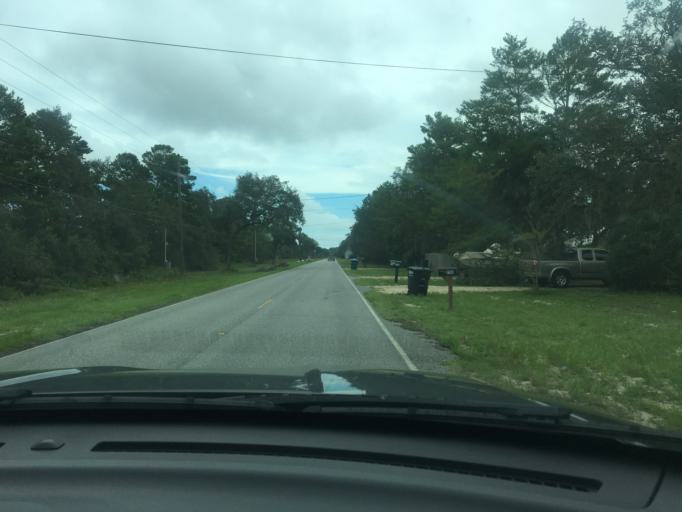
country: US
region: Florida
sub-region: Wakulla County
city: Crawfordville
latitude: 29.9082
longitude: -84.3588
